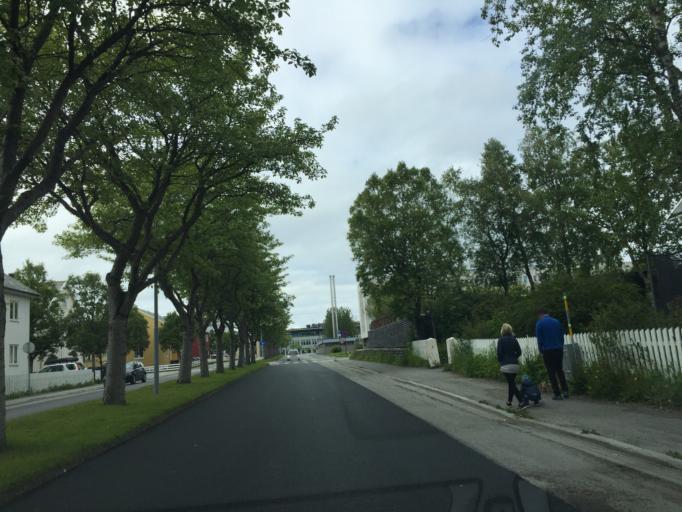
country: NO
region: Nordland
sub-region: Bodo
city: Bodo
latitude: 67.2790
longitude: 14.3775
